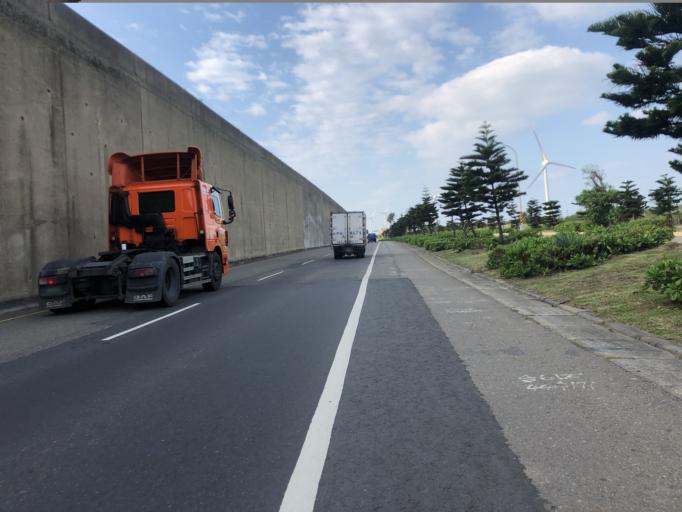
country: TW
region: Taiwan
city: Taoyuan City
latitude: 25.0506
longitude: 121.0864
